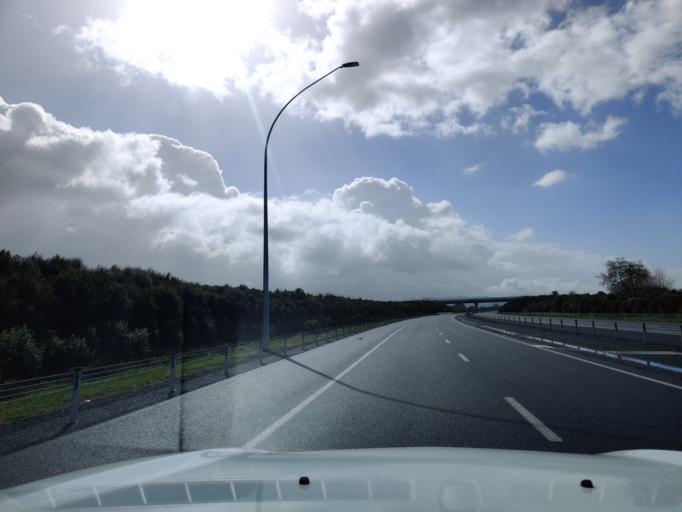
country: NZ
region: Waikato
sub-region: Waipa District
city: Cambridge
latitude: -37.8685
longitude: 175.4679
